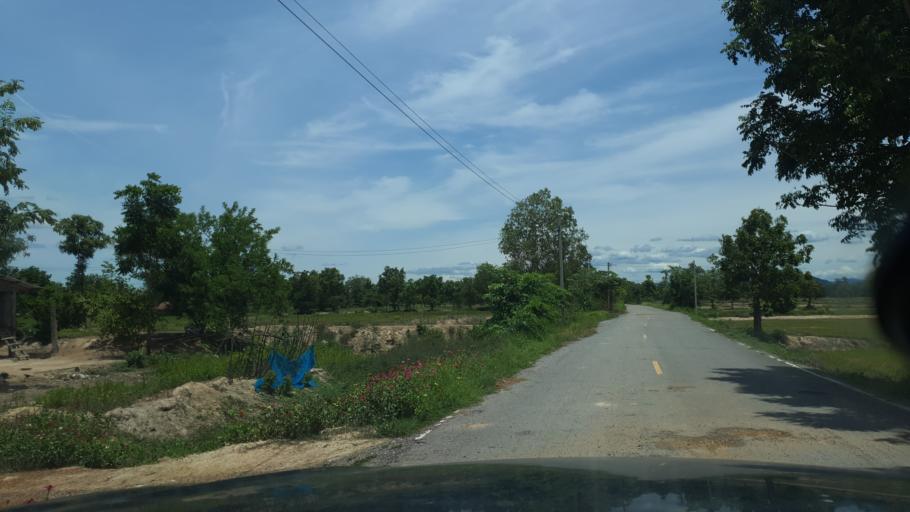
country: TH
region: Sukhothai
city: Ban Dan Lan Hoi
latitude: 17.1503
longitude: 99.6350
